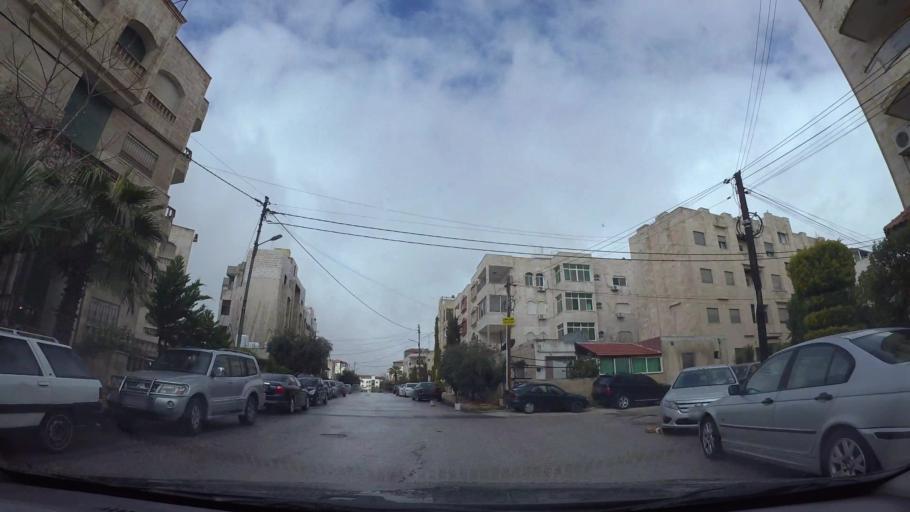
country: JO
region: Amman
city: Wadi as Sir
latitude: 31.9722
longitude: 35.8586
